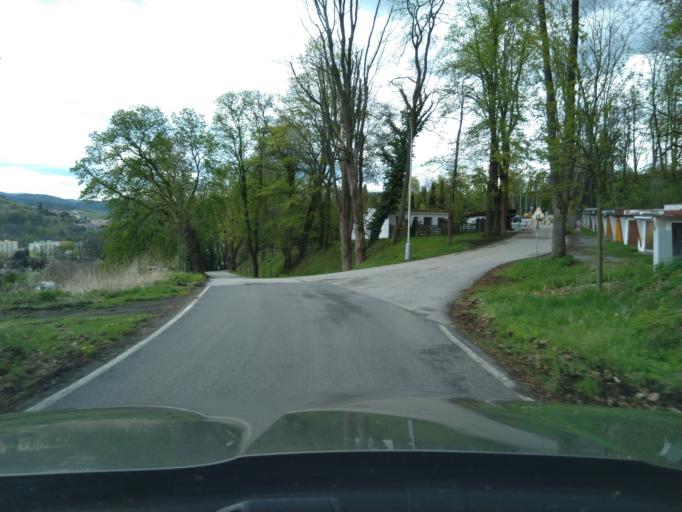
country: CZ
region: Jihocesky
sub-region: Okres Prachatice
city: Vimperk
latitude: 49.0573
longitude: 13.7721
